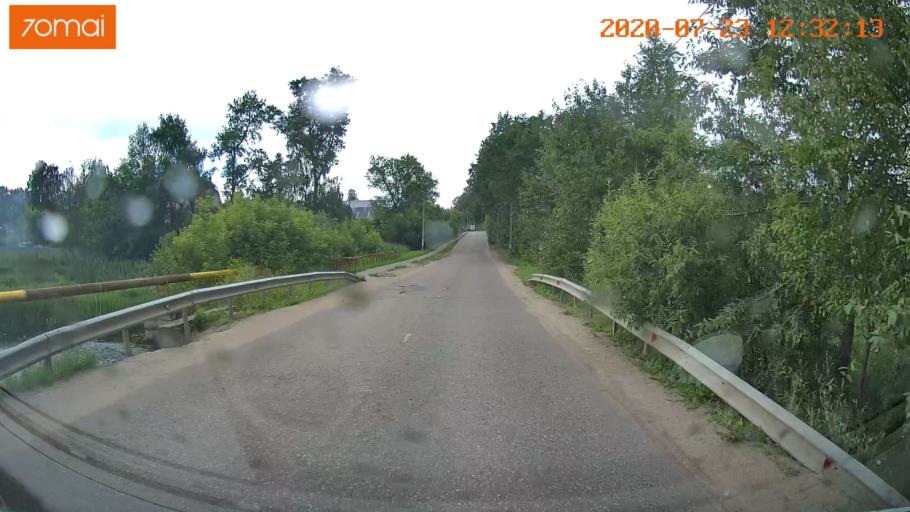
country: RU
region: Ivanovo
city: Bogorodskoye
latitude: 57.0459
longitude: 41.0094
